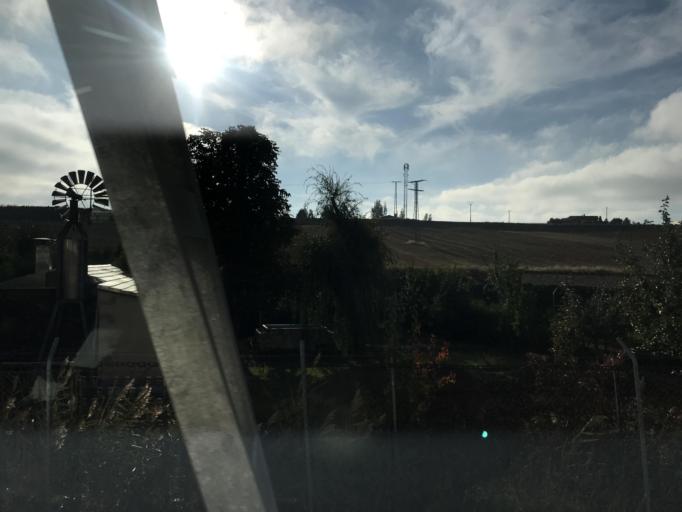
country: ES
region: Castille and Leon
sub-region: Provincia de Burgos
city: San Mames de Burgos
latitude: 42.3334
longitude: -3.8034
